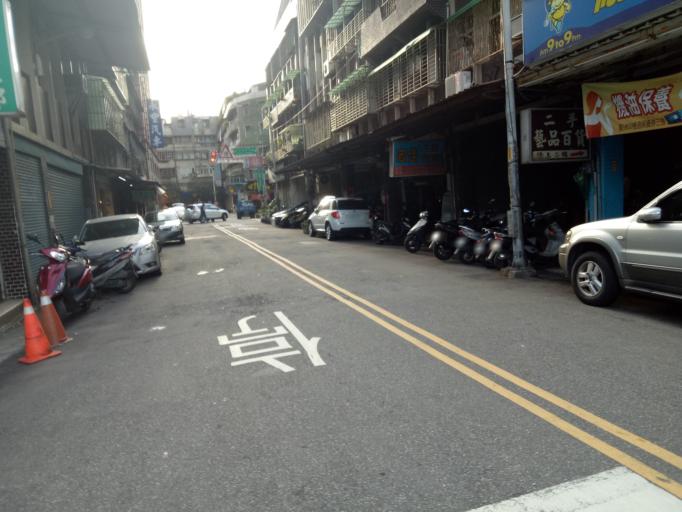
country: TW
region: Taipei
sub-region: Taipei
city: Banqiao
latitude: 25.0475
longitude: 121.4528
